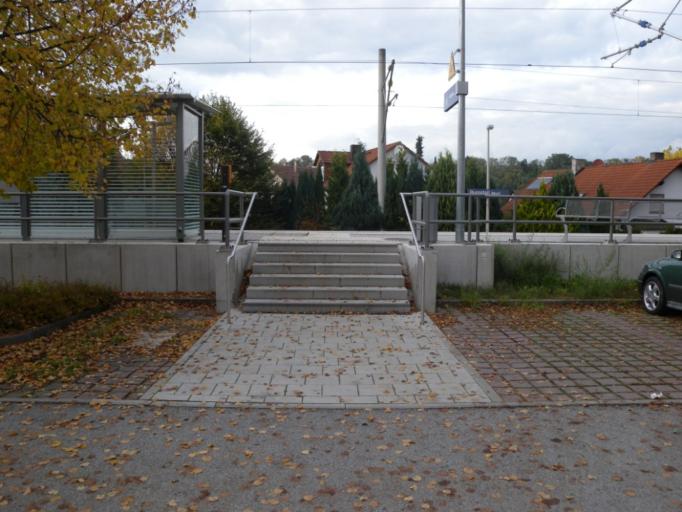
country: DE
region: Baden-Wuerttemberg
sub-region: Regierungsbezirk Stuttgart
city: Burgstetten
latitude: 48.9287
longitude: 9.3706
